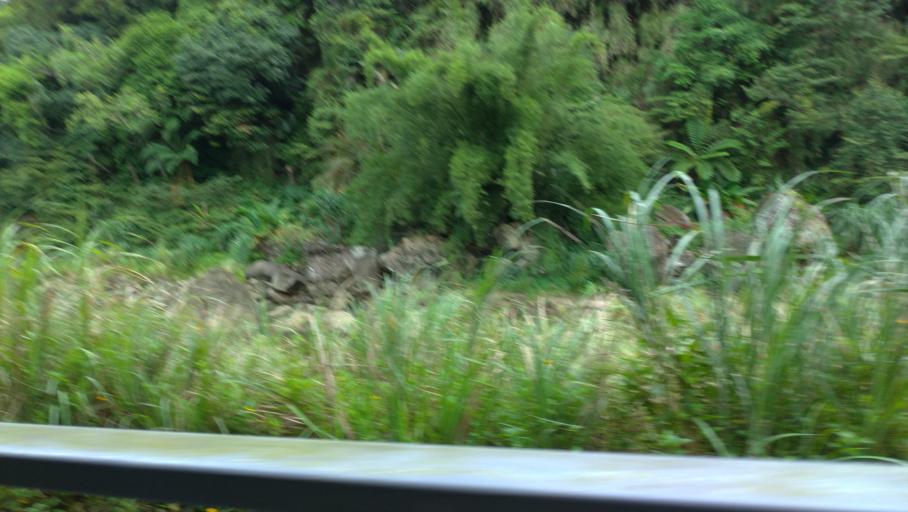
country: TW
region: Taiwan
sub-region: Keelung
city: Keelung
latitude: 25.0480
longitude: 121.7848
